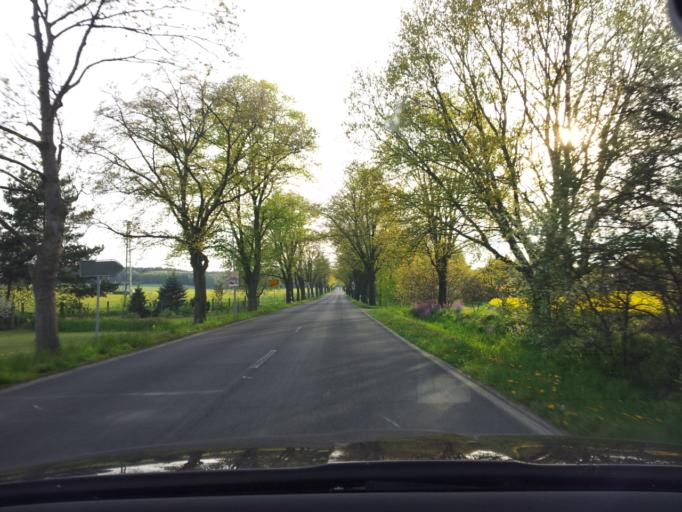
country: DE
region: Brandenburg
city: Drahnsdorf
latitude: 51.8538
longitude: 13.6027
